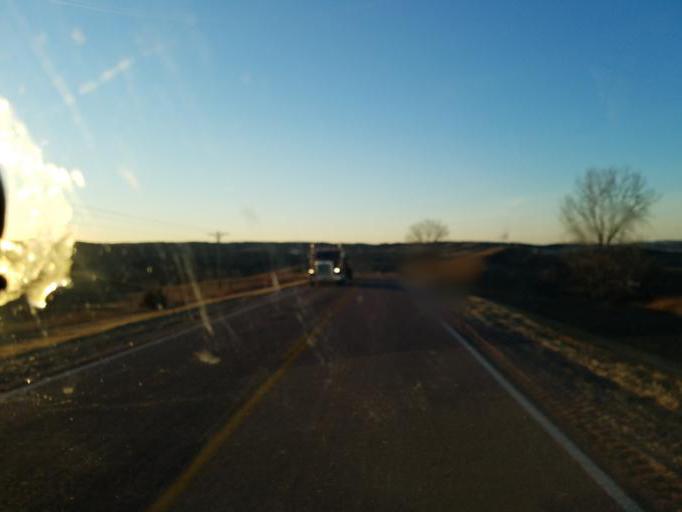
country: US
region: South Dakota
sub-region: Bon Homme County
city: Springfield
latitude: 42.7419
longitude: -97.9213
